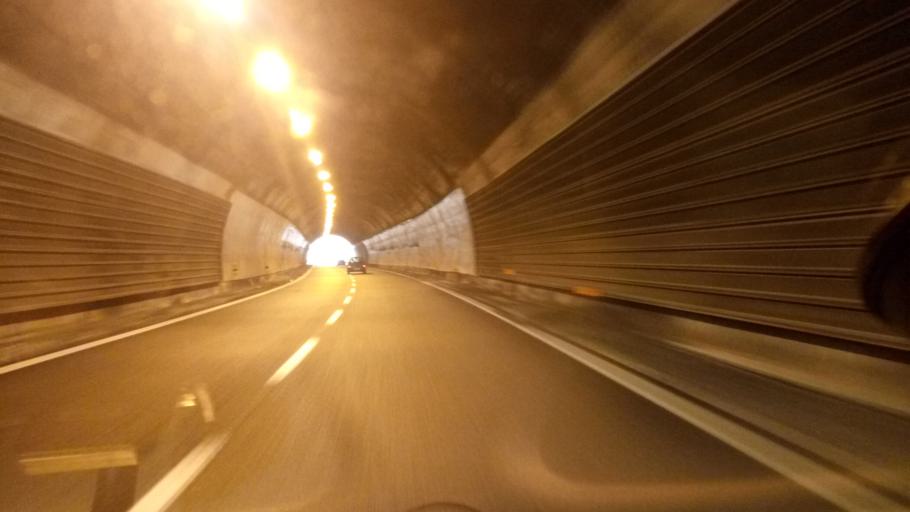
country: IT
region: Liguria
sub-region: Provincia di Genova
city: Mele
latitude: 44.4329
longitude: 8.7898
